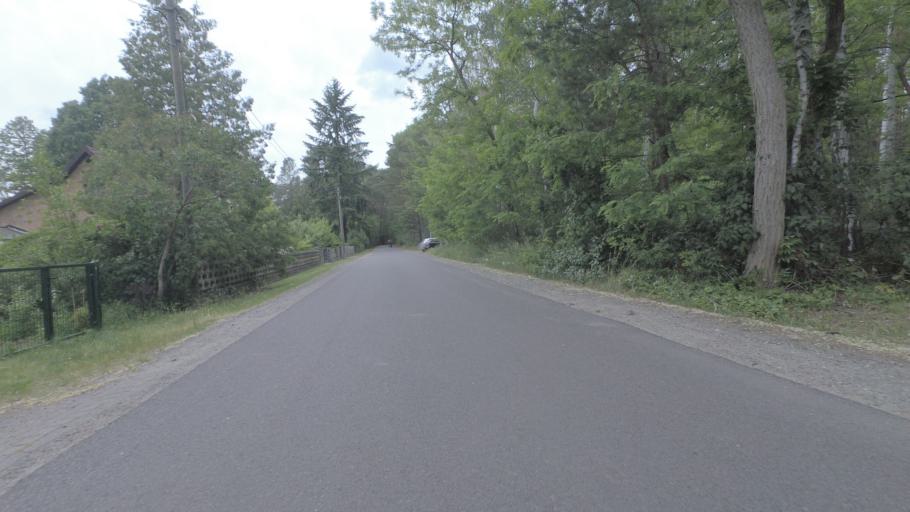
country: DE
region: Brandenburg
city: Bestensee
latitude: 52.2662
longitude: 13.7612
